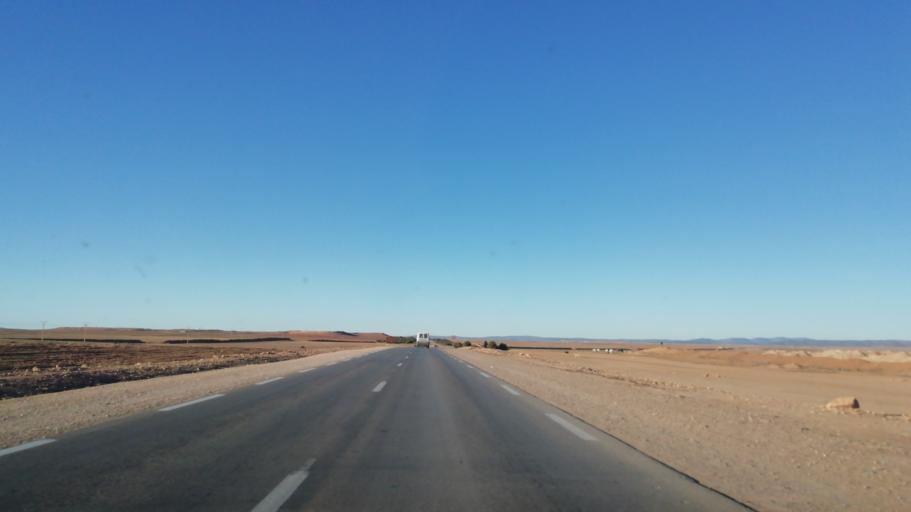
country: DZ
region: Tlemcen
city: Sebdou
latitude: 34.4859
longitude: -1.2725
